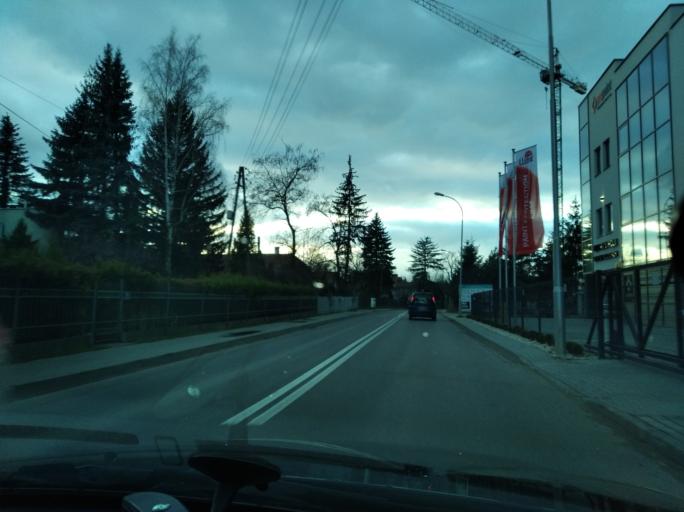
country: PL
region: Subcarpathian Voivodeship
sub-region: Rzeszow
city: Rzeszow
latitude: 50.0266
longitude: 22.0385
